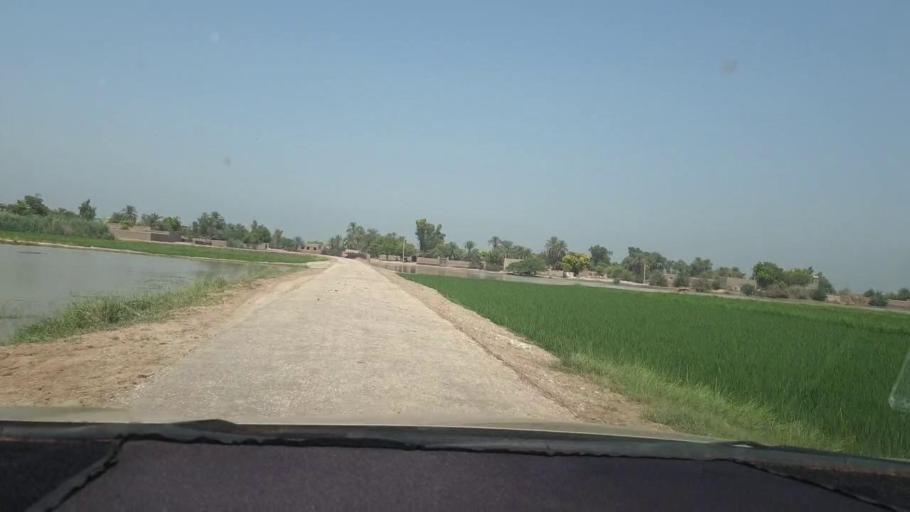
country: PK
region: Sindh
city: Kambar
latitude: 27.6227
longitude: 68.0526
